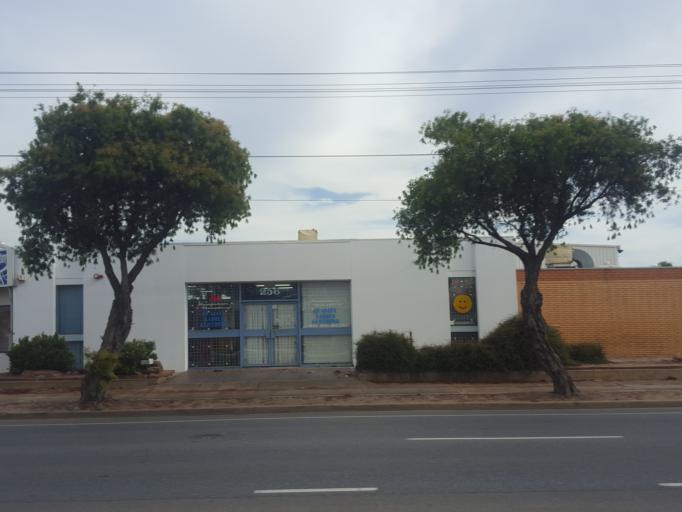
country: AU
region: South Australia
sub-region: Charles Sturt
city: Woodville North
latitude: -34.8507
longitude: 138.5424
